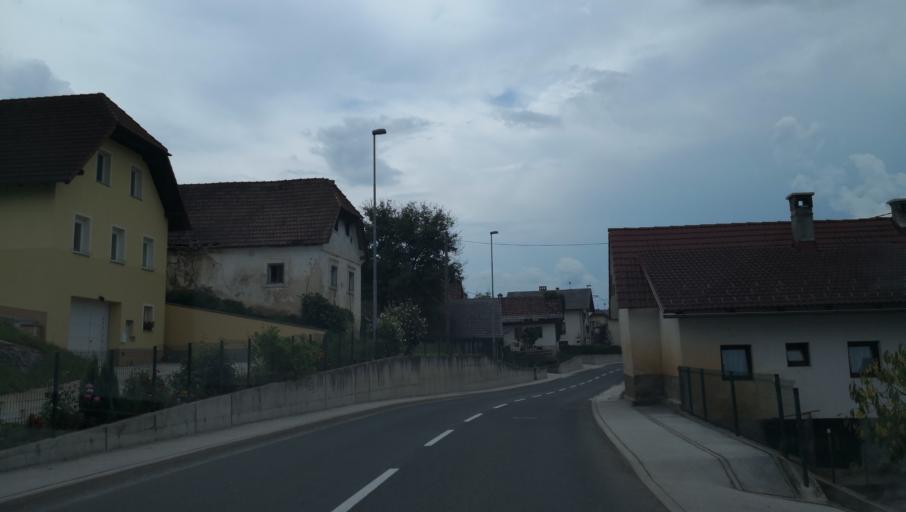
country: SI
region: Zuzemberk
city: Zuzemberk
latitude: 45.8376
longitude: 14.9180
